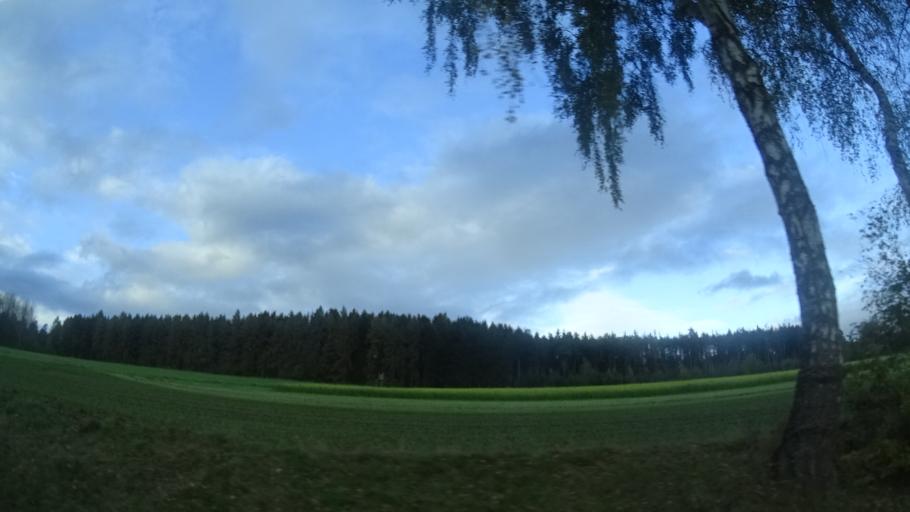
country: DE
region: Hesse
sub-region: Regierungsbezirk Kassel
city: Flieden
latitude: 50.4565
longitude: 9.5501
